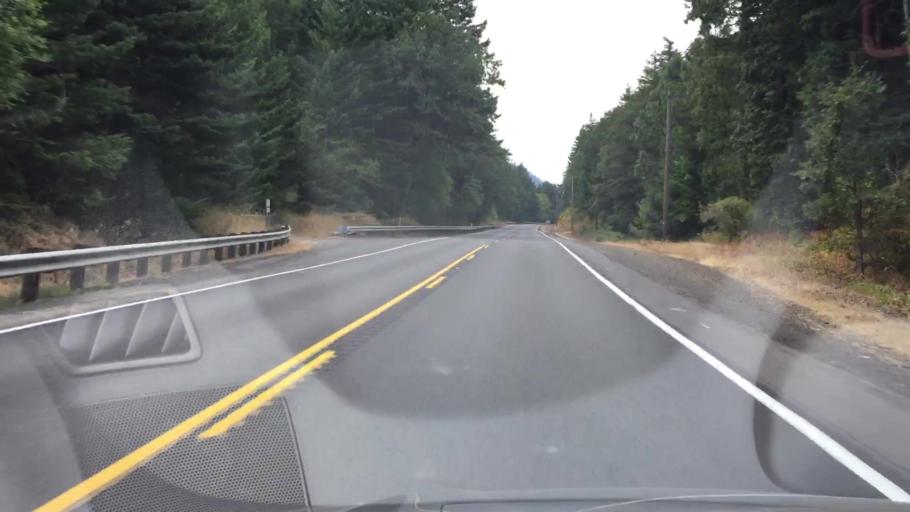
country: US
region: Washington
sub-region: Skamania County
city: Carson
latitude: 45.6994
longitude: -121.7303
